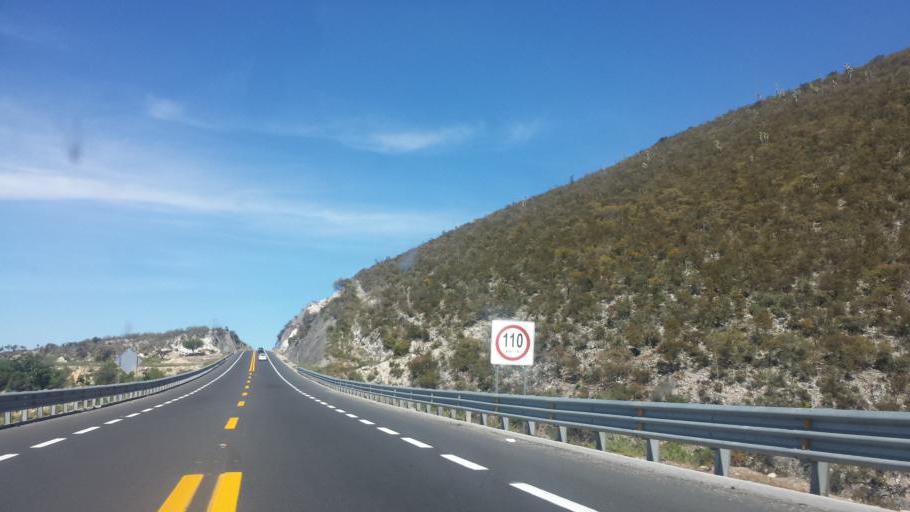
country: MX
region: Puebla
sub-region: San Jose Miahuatlan
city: San Pedro Tetitlan
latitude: 18.0031
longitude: -97.3553
